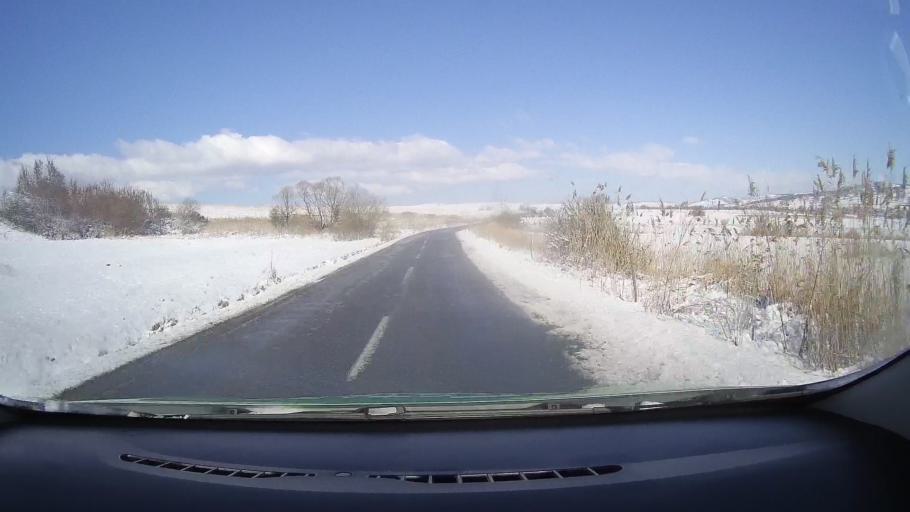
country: RO
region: Sibiu
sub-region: Comuna Rosia
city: Rosia
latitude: 45.8417
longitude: 24.3052
